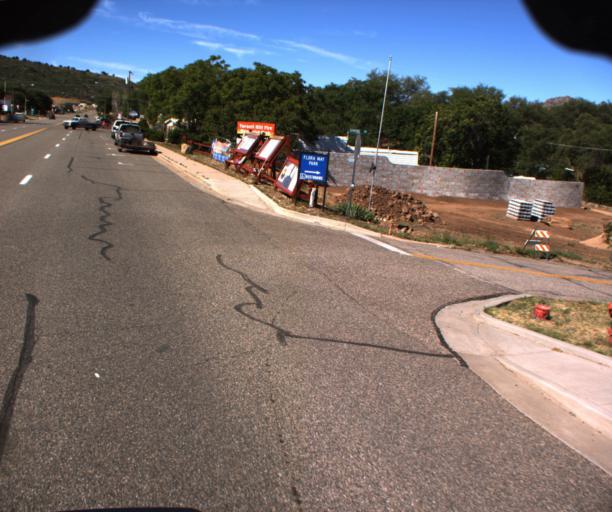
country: US
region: Arizona
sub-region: Yavapai County
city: Congress
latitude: 34.2227
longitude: -112.7467
